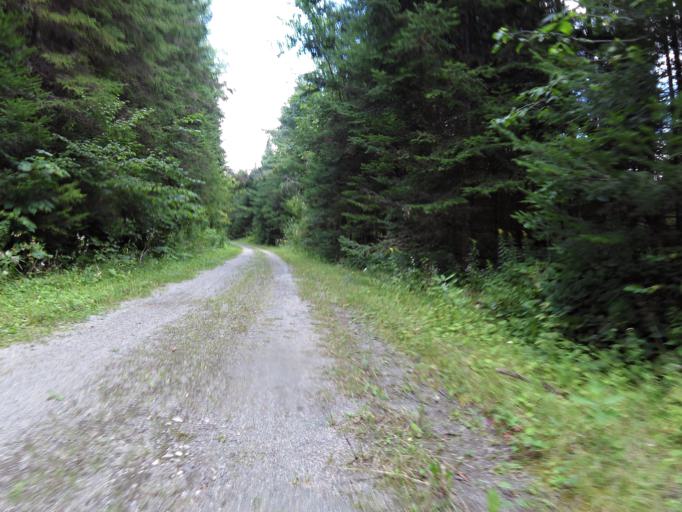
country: CA
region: Quebec
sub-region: Outaouais
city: Wakefield
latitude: 45.8574
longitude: -75.9926
